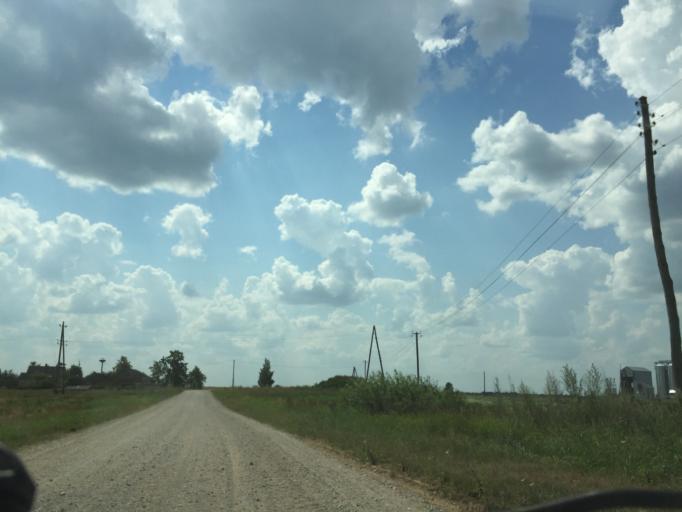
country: LT
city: Zagare
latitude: 56.3366
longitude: 23.0816
